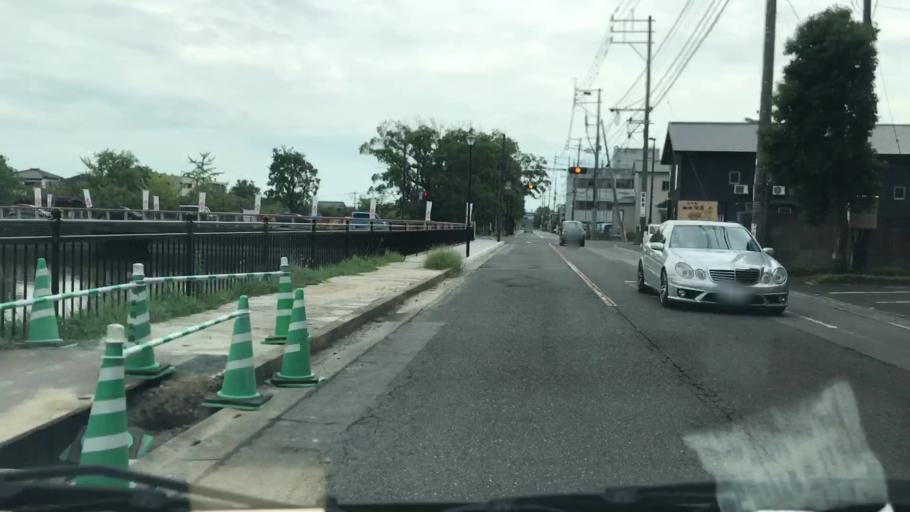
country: JP
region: Saga Prefecture
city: Saga-shi
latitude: 33.2461
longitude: 130.2959
